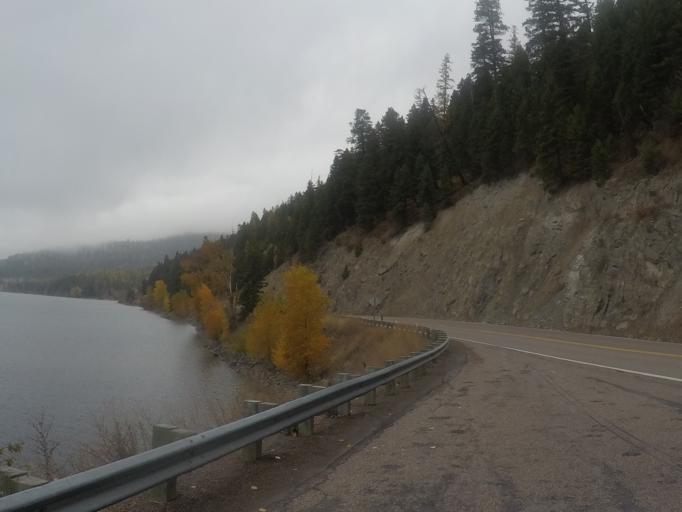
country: US
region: Montana
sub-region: Flathead County
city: Bigfork
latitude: 47.9409
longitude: -113.8710
